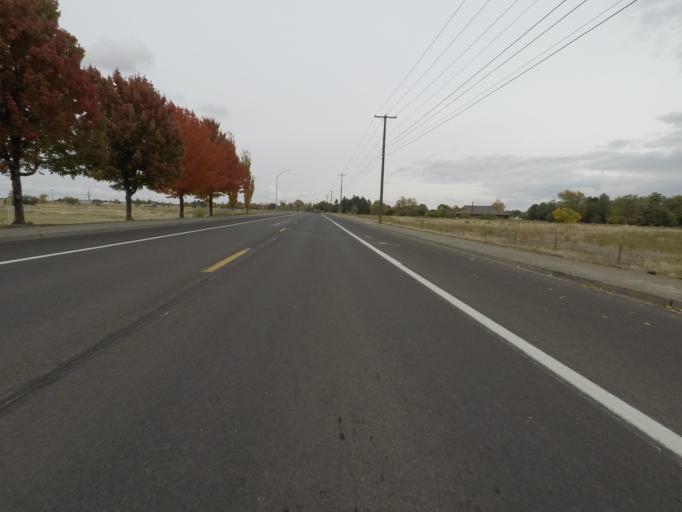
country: US
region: Washington
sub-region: Walla Walla County
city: Walla Walla East
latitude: 46.0724
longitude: -118.2874
